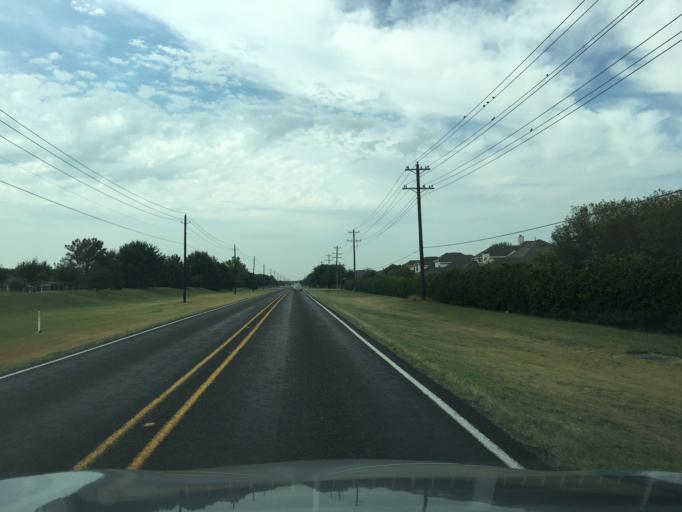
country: US
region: Texas
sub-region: Collin County
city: Parker
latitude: 33.0813
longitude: -96.6202
